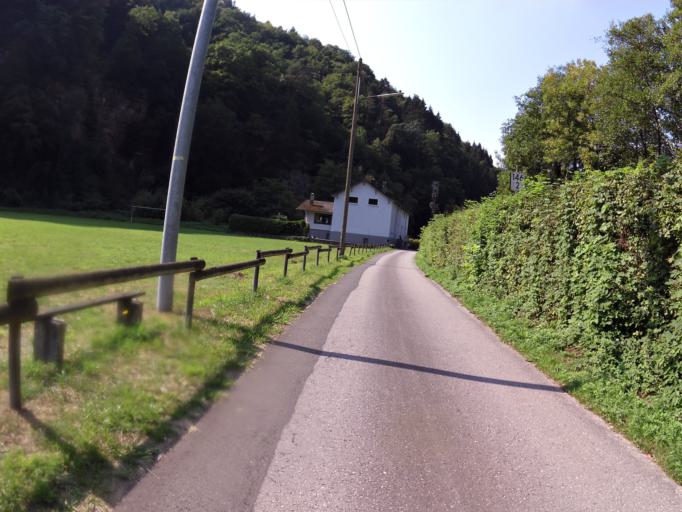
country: DE
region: Rheinland-Pfalz
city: Hosten
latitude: 49.8997
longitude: 6.6127
